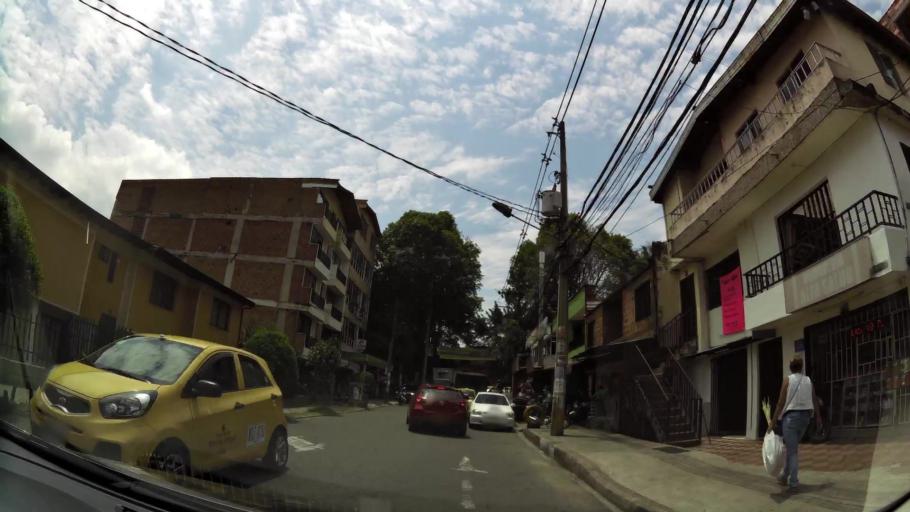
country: CO
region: Antioquia
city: Bello
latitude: 6.3115
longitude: -75.5700
